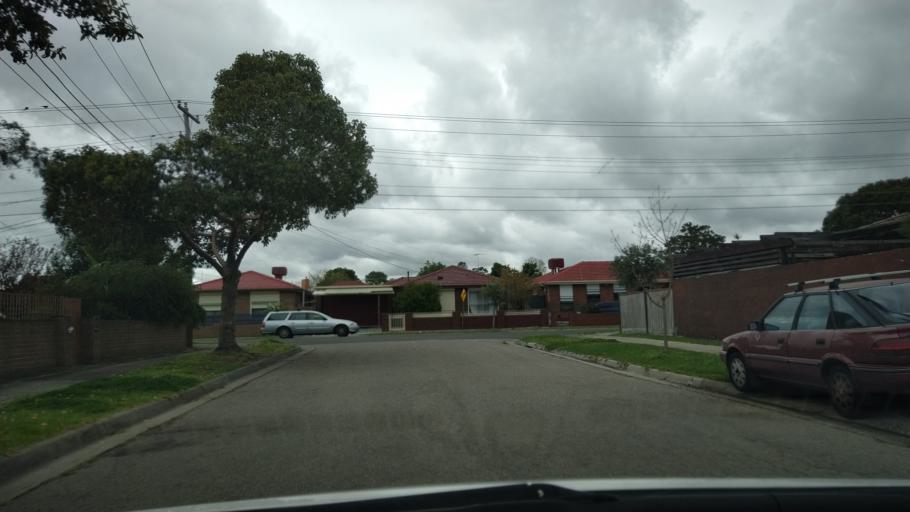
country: AU
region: Victoria
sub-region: Greater Dandenong
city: Keysborough
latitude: -37.9832
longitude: 145.1729
